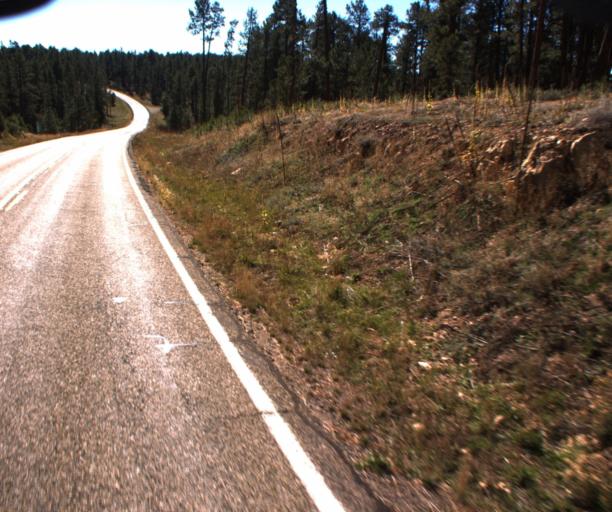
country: US
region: Arizona
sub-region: Coconino County
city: Fredonia
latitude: 36.7407
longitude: -112.2297
